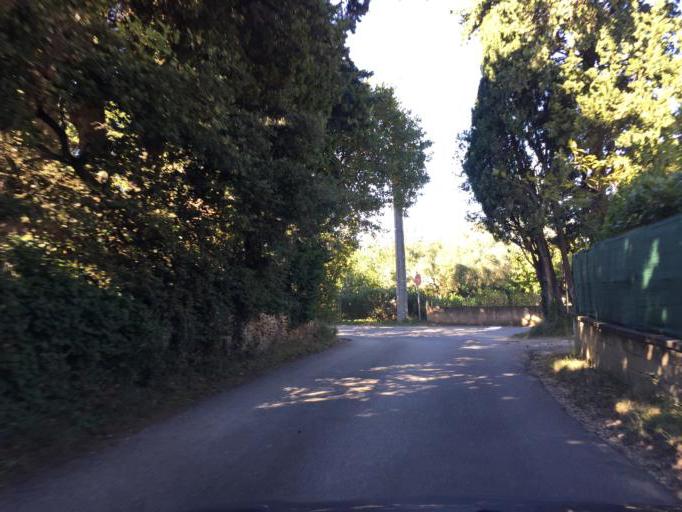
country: FR
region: Provence-Alpes-Cote d'Azur
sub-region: Departement du Vaucluse
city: Piolenc
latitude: 44.1755
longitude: 4.7720
